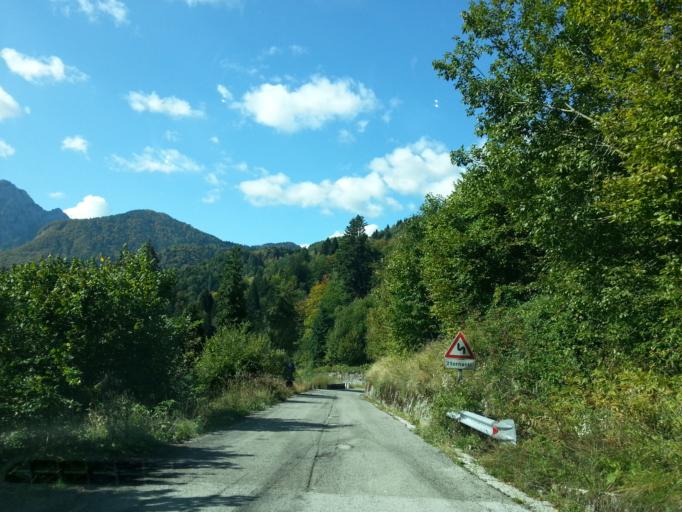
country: IT
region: Friuli Venezia Giulia
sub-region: Provincia di Udine
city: Moggio Udinese
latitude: 46.4963
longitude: 13.2179
